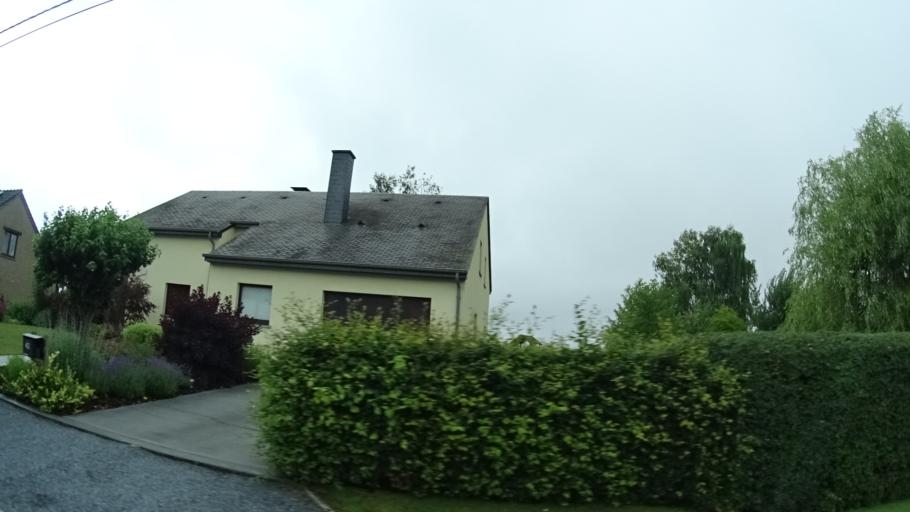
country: BE
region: Wallonia
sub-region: Province du Luxembourg
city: Habay-la-Vieille
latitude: 49.7294
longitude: 5.6190
